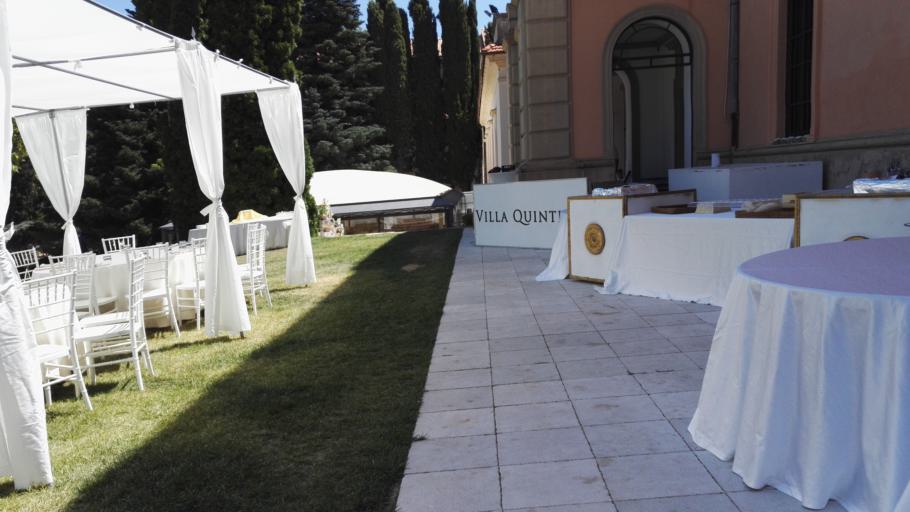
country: IT
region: Calabria
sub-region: Provincia di Cosenza
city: Carolei
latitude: 39.2488
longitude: 16.2190
